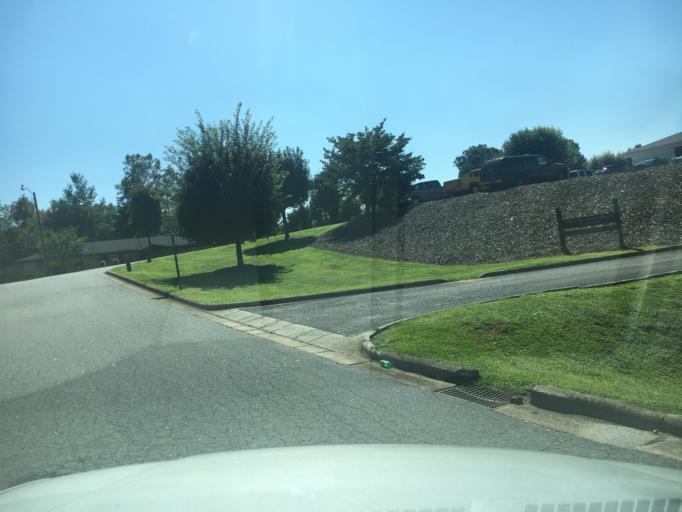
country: US
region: North Carolina
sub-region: McDowell County
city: West Marion
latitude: 35.6662
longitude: -82.0245
